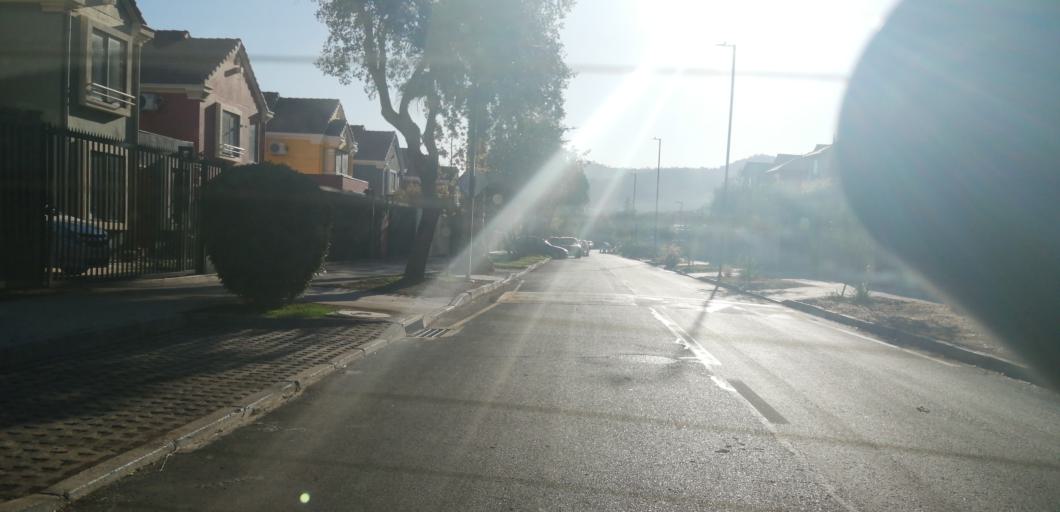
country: CL
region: Santiago Metropolitan
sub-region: Provincia de Santiago
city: Lo Prado
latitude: -33.4519
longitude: -70.8444
